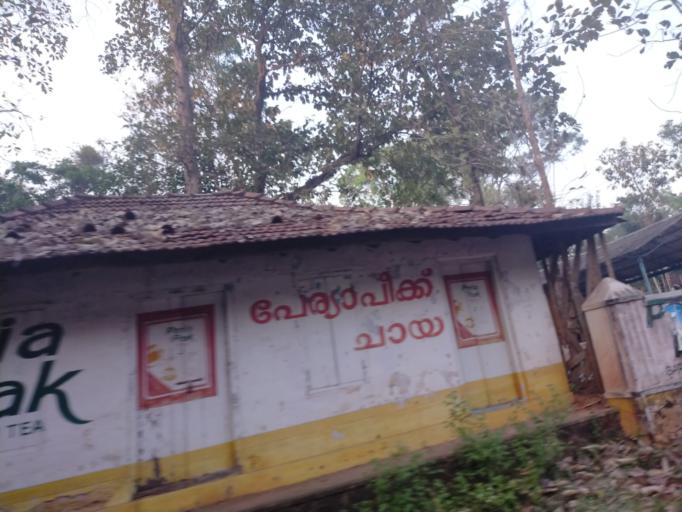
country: IN
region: Kerala
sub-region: Kottayam
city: Palackattumala
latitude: 9.7377
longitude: 76.5129
